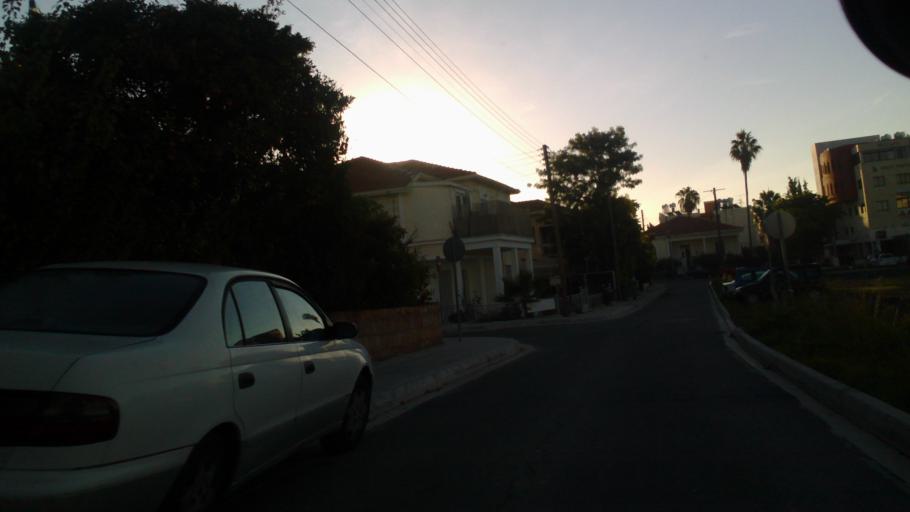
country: CY
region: Pafos
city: Paphos
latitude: 34.7779
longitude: 32.4283
